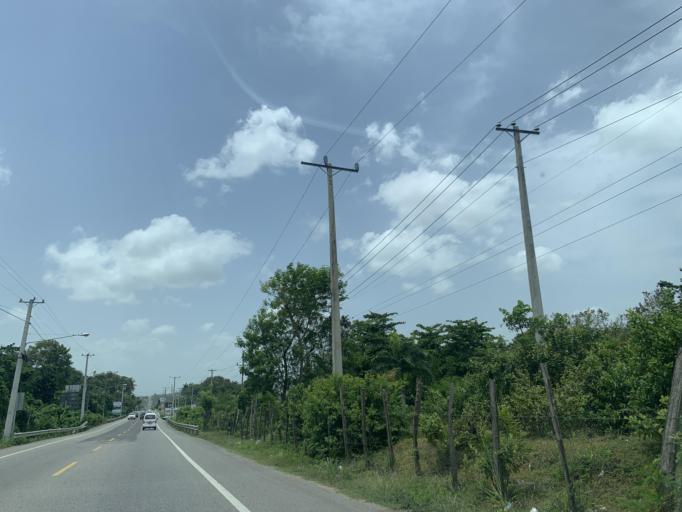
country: DO
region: Puerto Plata
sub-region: Puerto Plata
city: Puerto Plata
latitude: 19.7519
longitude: -70.6409
